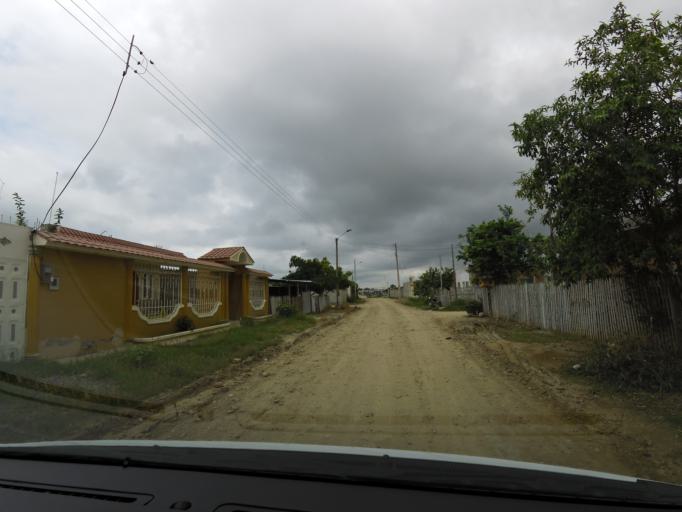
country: EC
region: El Oro
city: Huaquillas
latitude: -3.4833
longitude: -80.2064
